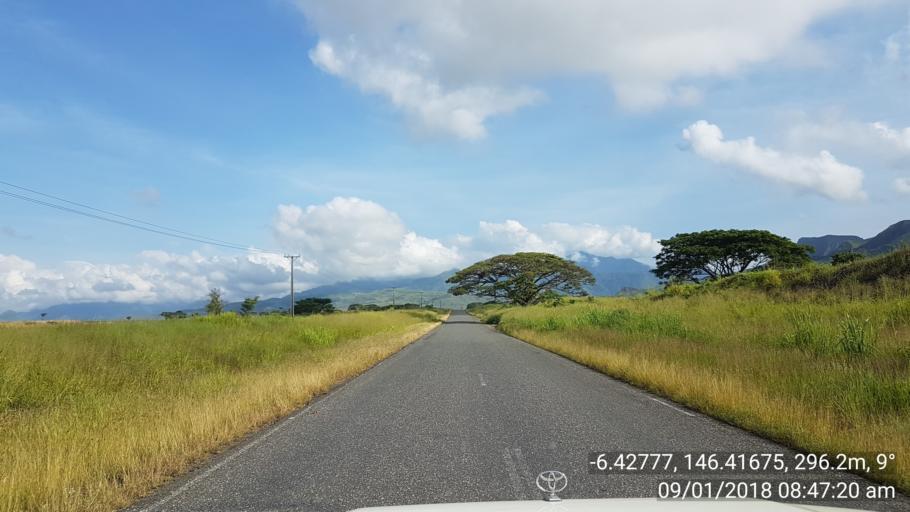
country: PG
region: Eastern Highlands
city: Kainantu
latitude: -6.4281
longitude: 146.4167
